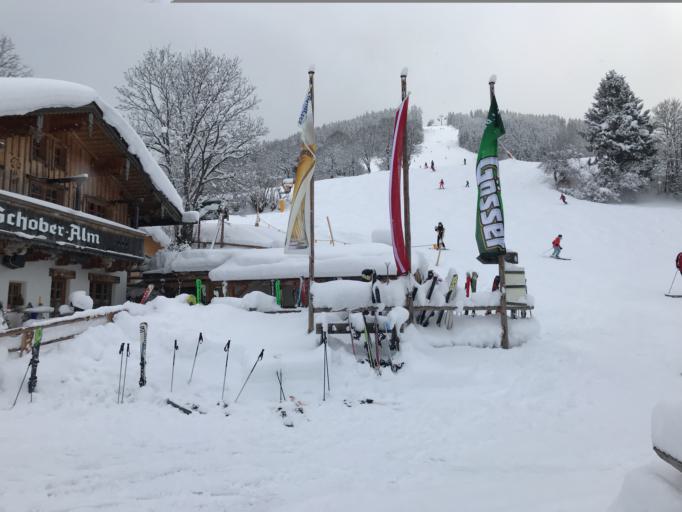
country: AT
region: Salzburg
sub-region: Politischer Bezirk Zell am See
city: Zell am See
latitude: 47.3012
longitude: 12.7794
